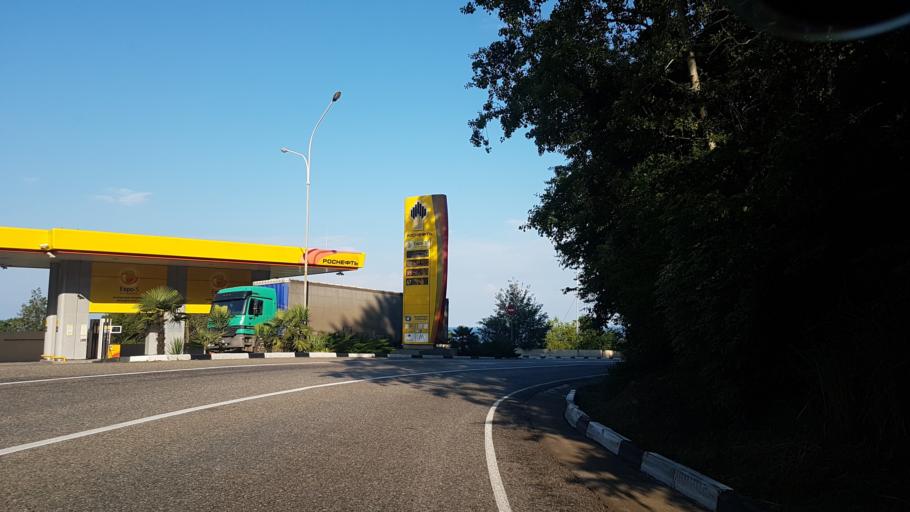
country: RU
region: Krasnodarskiy
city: Vardane
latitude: 43.7589
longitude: 39.5119
